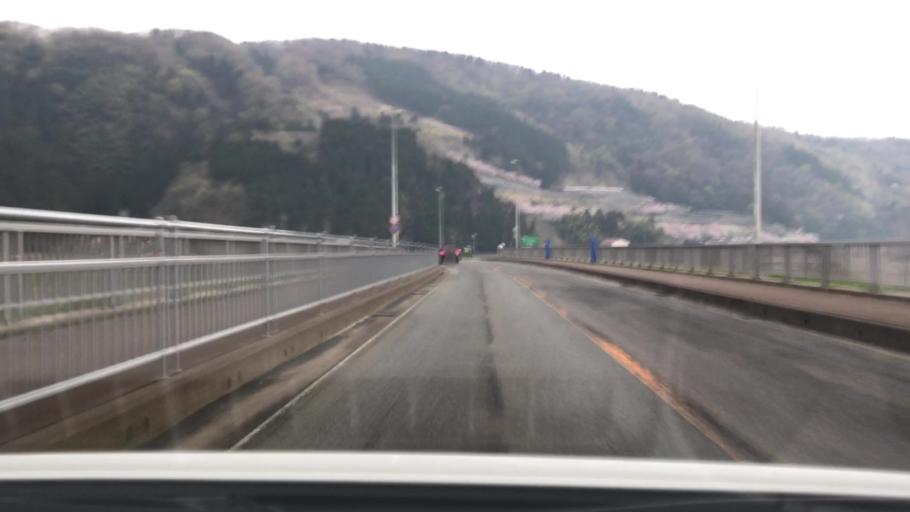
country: JP
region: Fukui
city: Fukui-shi
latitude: 36.0880
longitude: 136.1853
